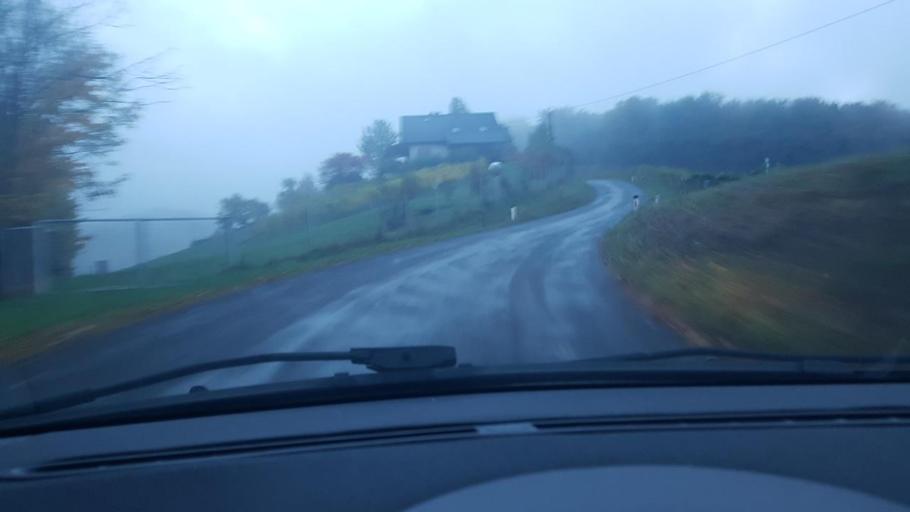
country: AT
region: Styria
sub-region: Politischer Bezirk Leibnitz
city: Sulztal an der Weinstrasse
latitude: 46.6626
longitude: 15.5402
